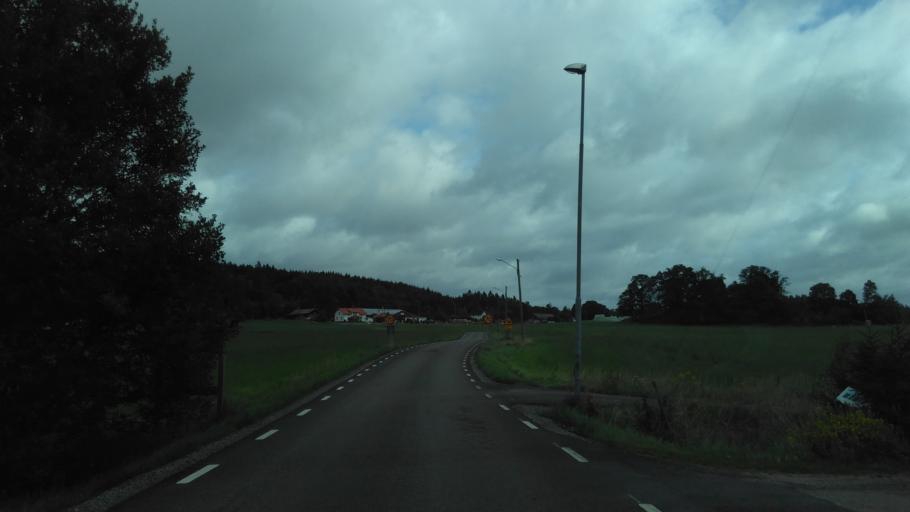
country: SE
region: Vaestra Goetaland
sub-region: Marks Kommun
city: Fritsla
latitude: 57.5682
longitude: 12.7839
